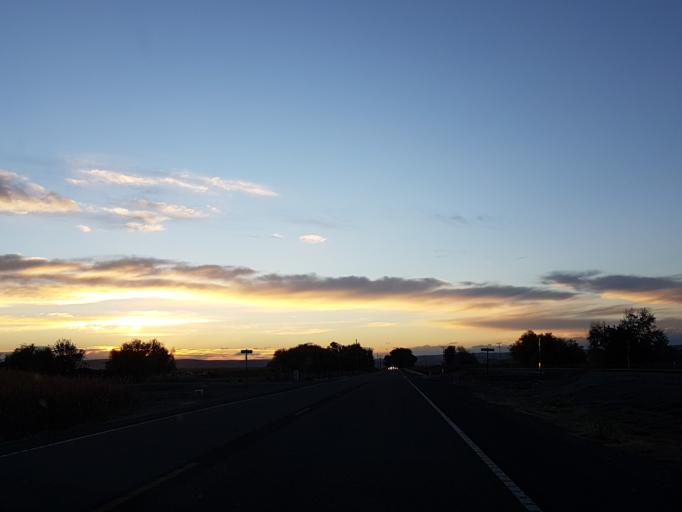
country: US
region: Oregon
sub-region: Malheur County
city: Vale
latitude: 43.9374
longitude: -117.3247
